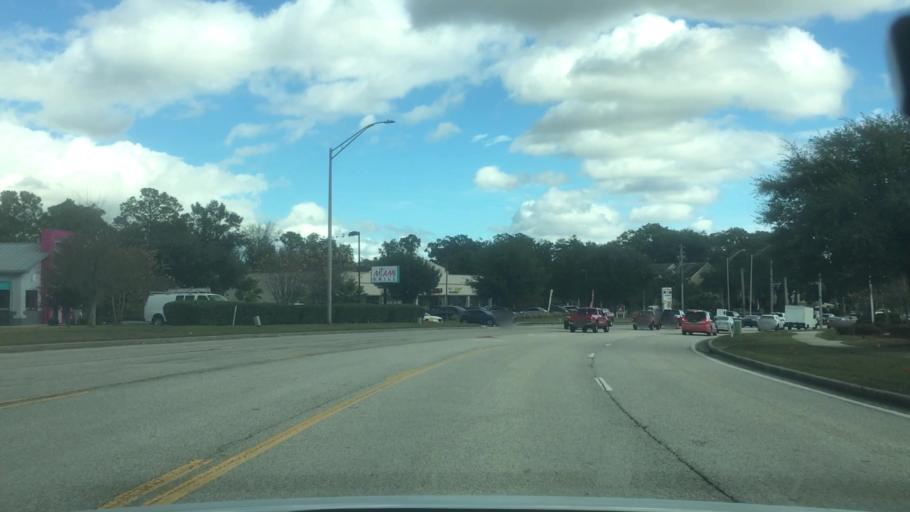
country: US
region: Florida
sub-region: Duval County
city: Jacksonville
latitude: 30.3304
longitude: -81.5487
